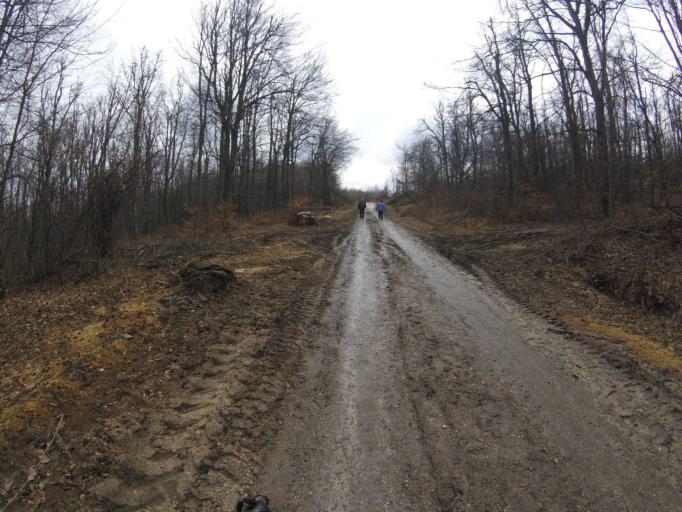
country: HU
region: Pest
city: Pilisszanto
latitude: 47.6938
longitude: 18.8664
